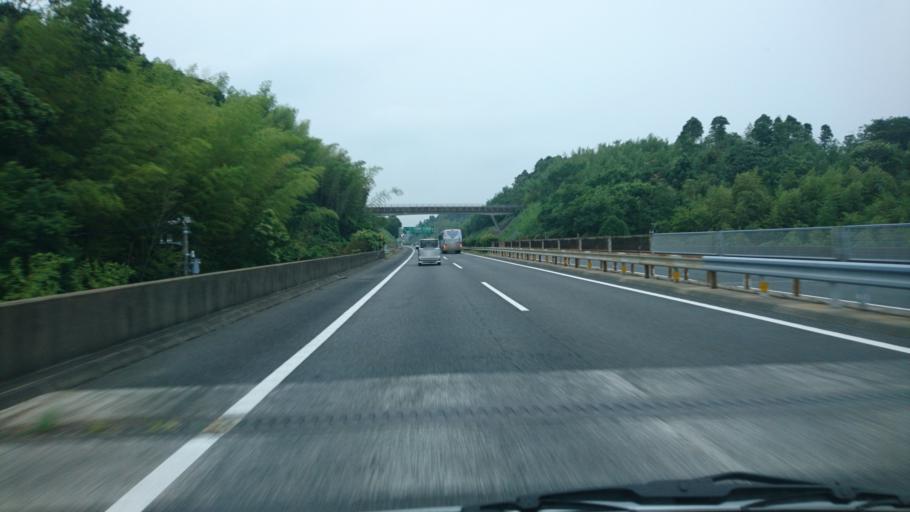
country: JP
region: Chiba
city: Narita
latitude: 35.7927
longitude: 140.3511
